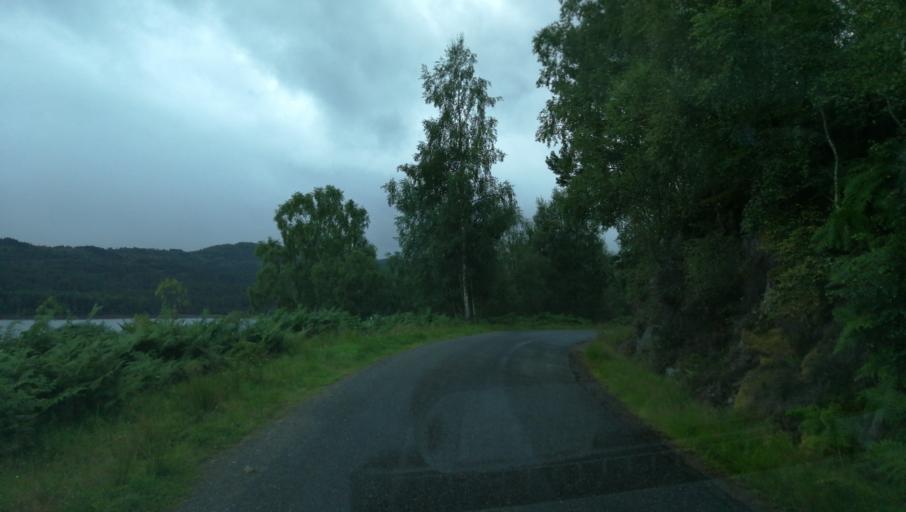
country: GB
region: Scotland
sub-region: Highland
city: Spean Bridge
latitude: 57.2858
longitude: -4.9215
